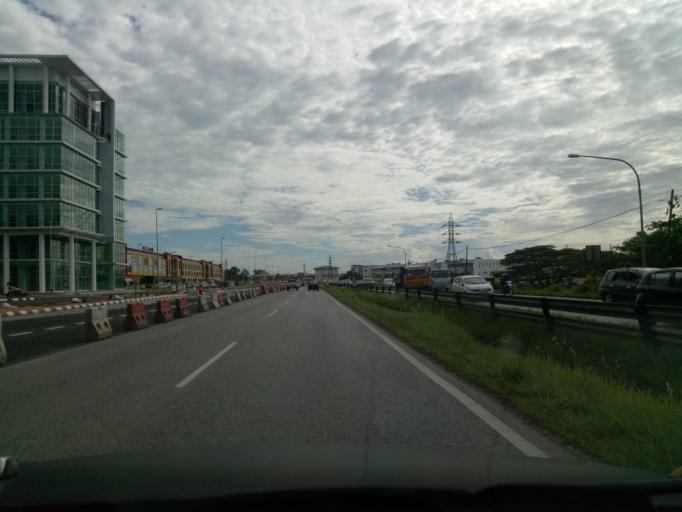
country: MY
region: Sarawak
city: Kuching
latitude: 1.4641
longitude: 110.3275
